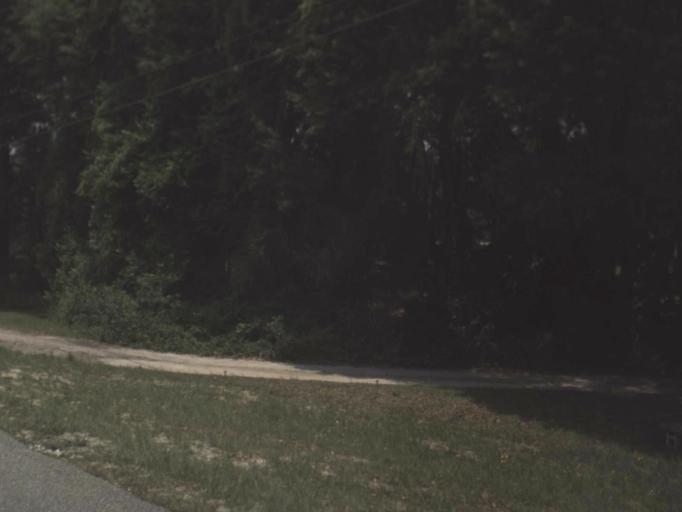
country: US
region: Florida
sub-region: Putnam County
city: Palatka
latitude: 29.6041
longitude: -81.7118
